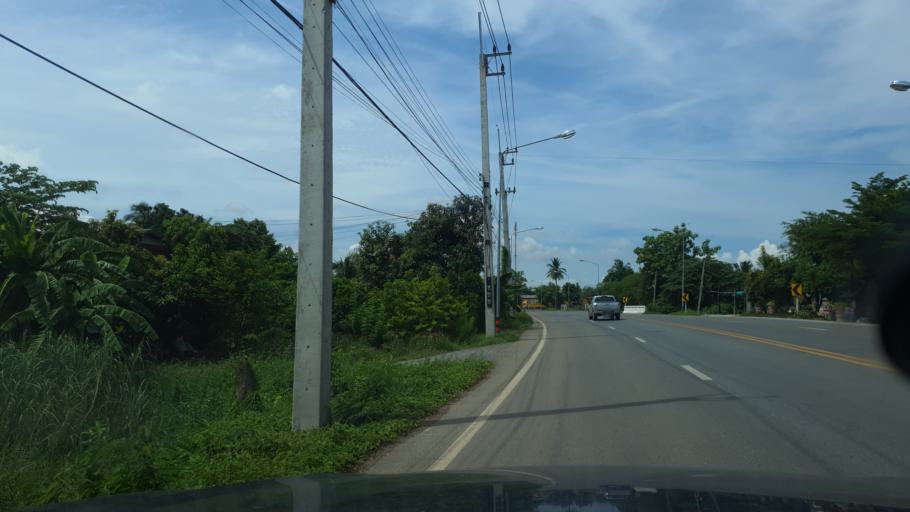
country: TH
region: Sukhothai
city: Sukhothai
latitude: 17.0479
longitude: 99.8163
